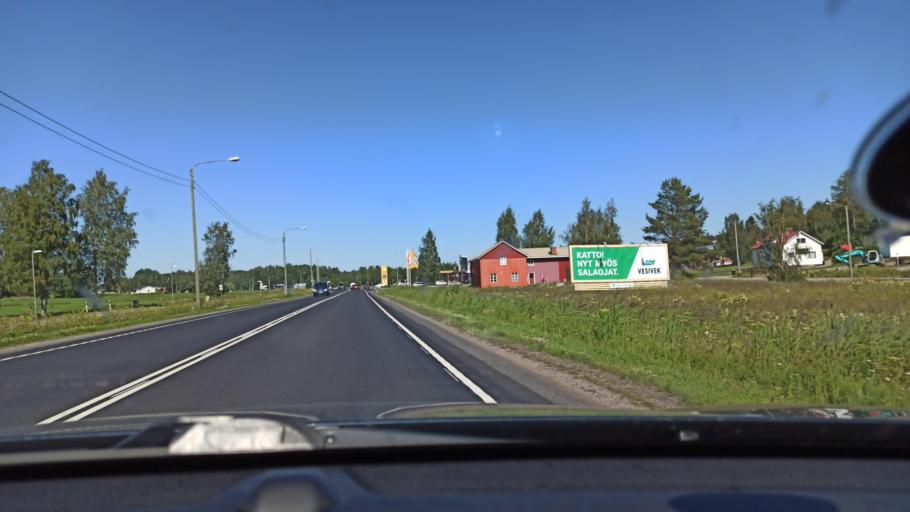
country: FI
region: Ostrobothnia
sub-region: Vaasa
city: Oravais
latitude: 63.3062
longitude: 22.3826
